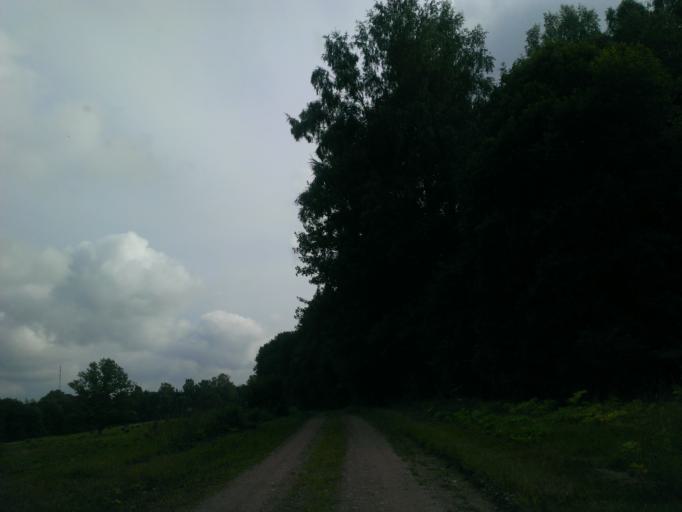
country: LV
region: Priekuli
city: Priekuli
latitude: 57.2623
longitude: 25.3919
